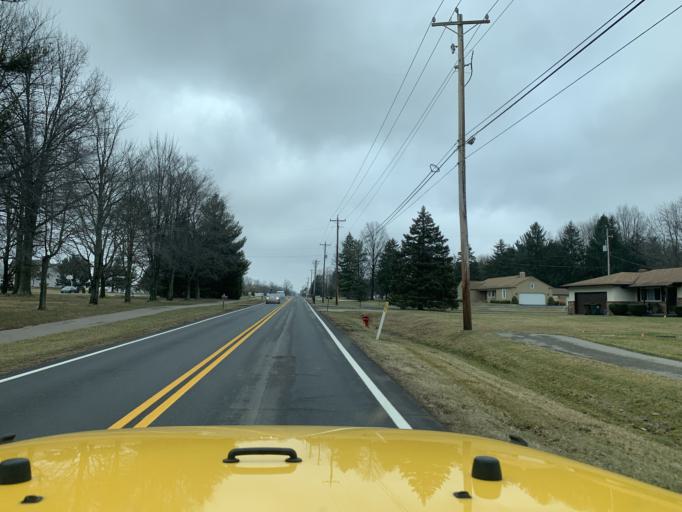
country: US
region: Ohio
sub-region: Franklin County
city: New Albany
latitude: 40.0978
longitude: -82.8093
